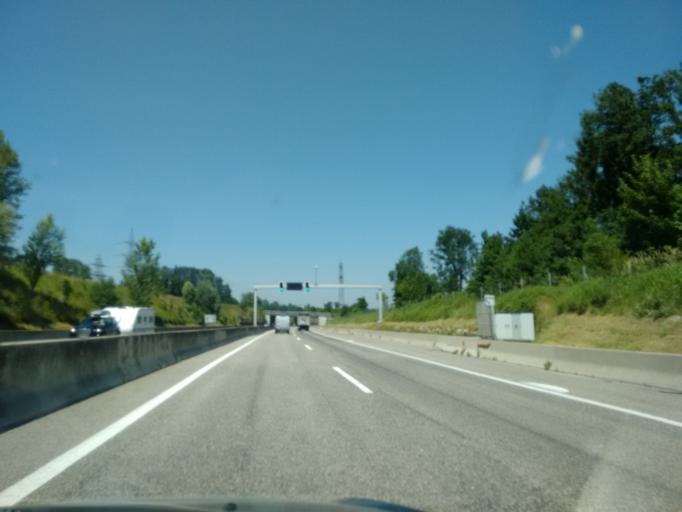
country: AT
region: Upper Austria
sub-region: Wels-Land
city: Steinhaus
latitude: 48.0822
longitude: 14.0194
